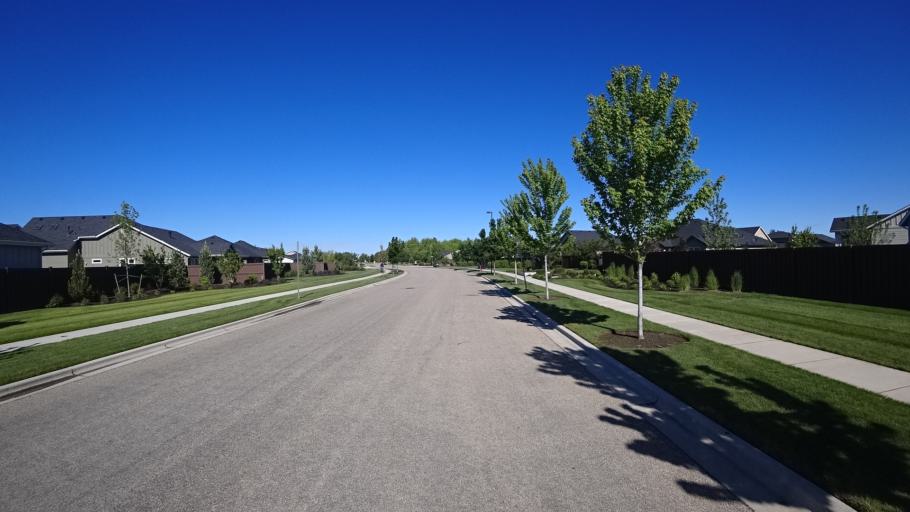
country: US
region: Idaho
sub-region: Ada County
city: Star
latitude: 43.6578
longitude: -116.4506
